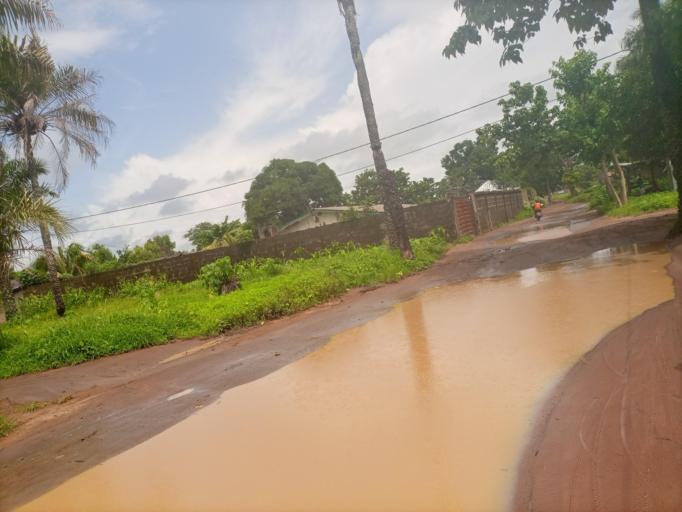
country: SL
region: Northern Province
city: Tintafor
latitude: 8.6349
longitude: -13.2167
